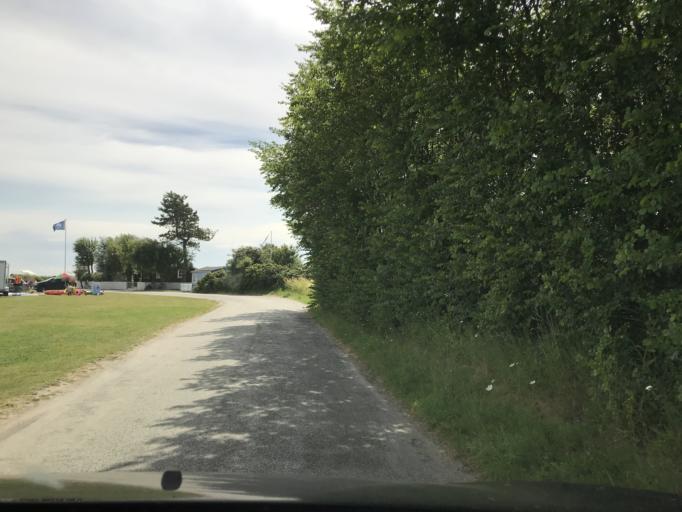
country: DK
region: South Denmark
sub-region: AEro Kommune
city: Marstal
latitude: 54.8451
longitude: 10.5199
